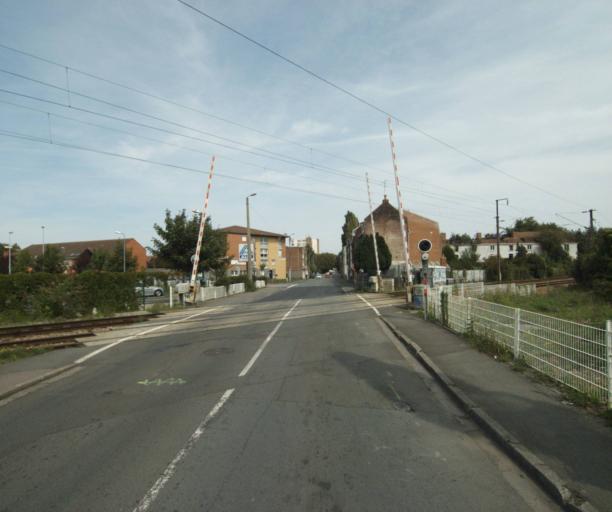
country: FR
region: Nord-Pas-de-Calais
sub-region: Departement du Nord
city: Loos
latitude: 50.6134
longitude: 3.0246
